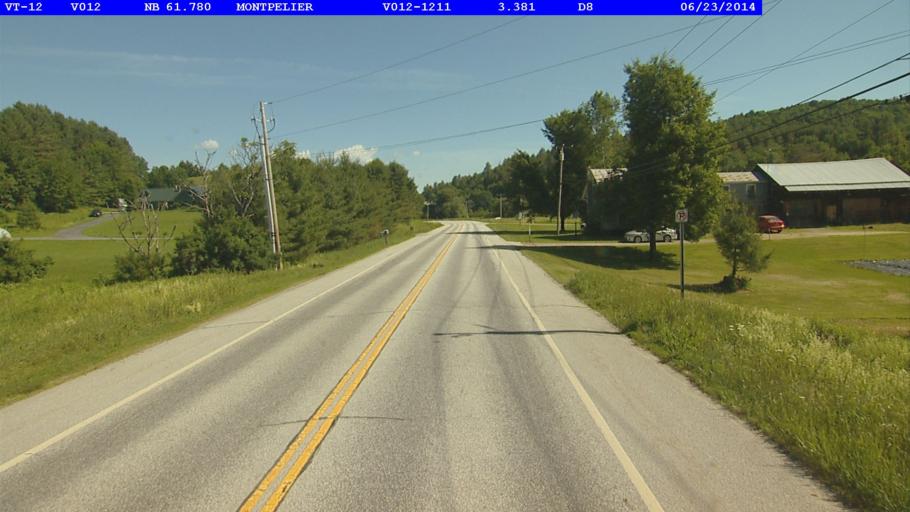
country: US
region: Vermont
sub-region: Washington County
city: Montpelier
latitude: 44.2905
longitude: -72.5790
